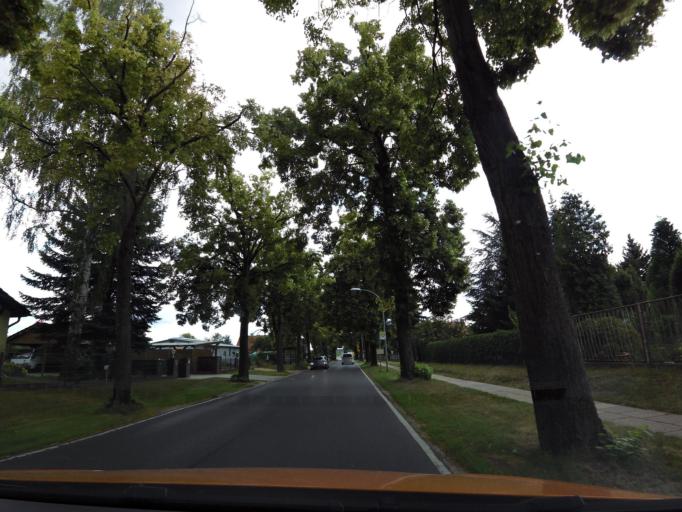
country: DE
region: Brandenburg
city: Rangsdorf
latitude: 52.3188
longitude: 13.4407
